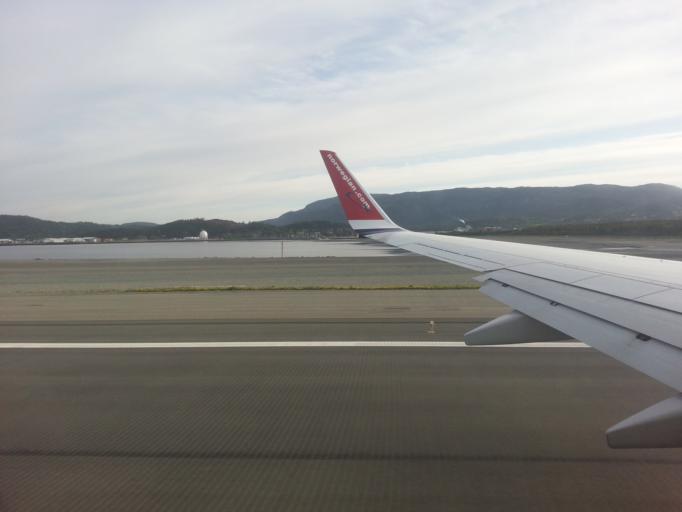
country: NO
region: Nord-Trondelag
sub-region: Stjordal
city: Stjordal
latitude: 63.4578
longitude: 10.8958
